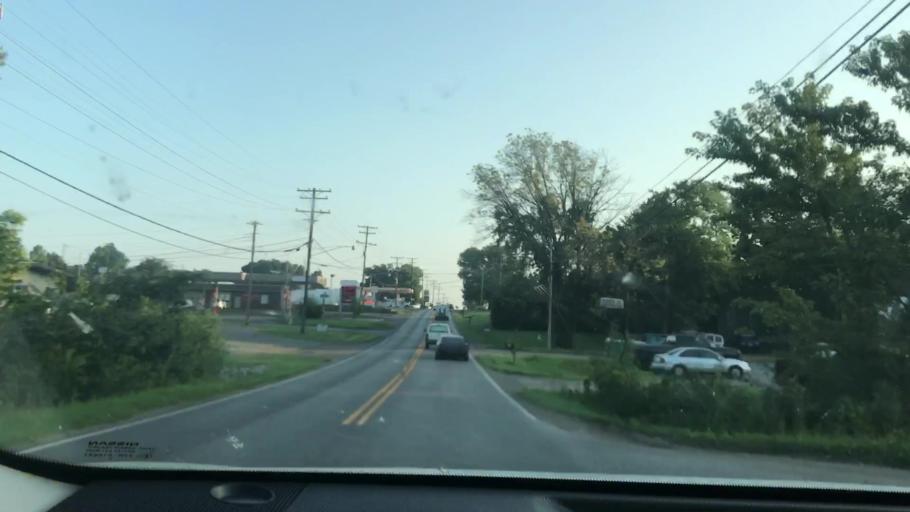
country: US
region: Kentucky
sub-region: Calloway County
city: Murray
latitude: 36.5989
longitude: -88.3033
